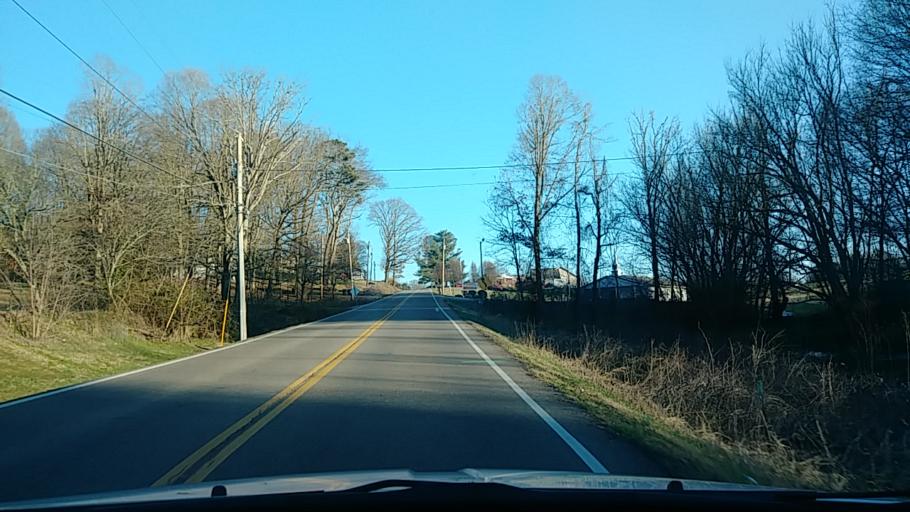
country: US
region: Tennessee
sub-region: Hamblen County
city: Morristown
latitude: 36.1873
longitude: -83.3793
